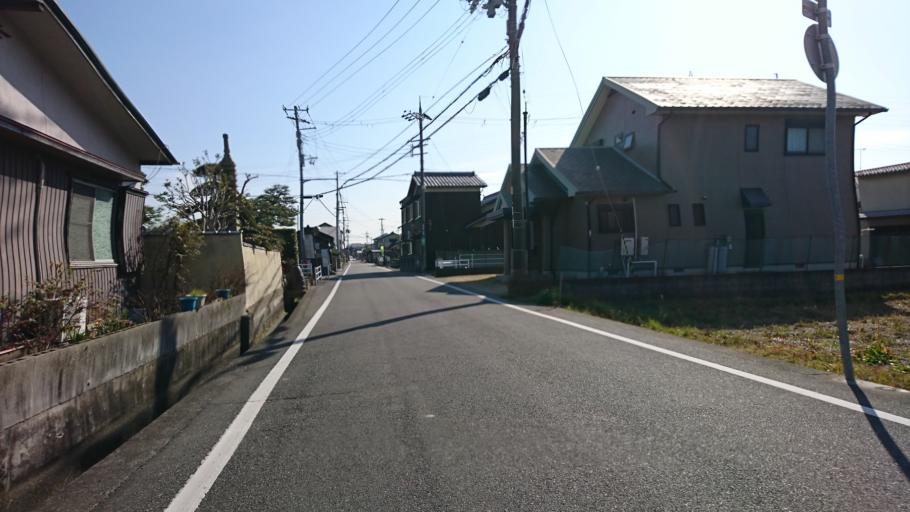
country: JP
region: Hyogo
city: Kakogawacho-honmachi
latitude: 34.7931
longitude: 134.8290
